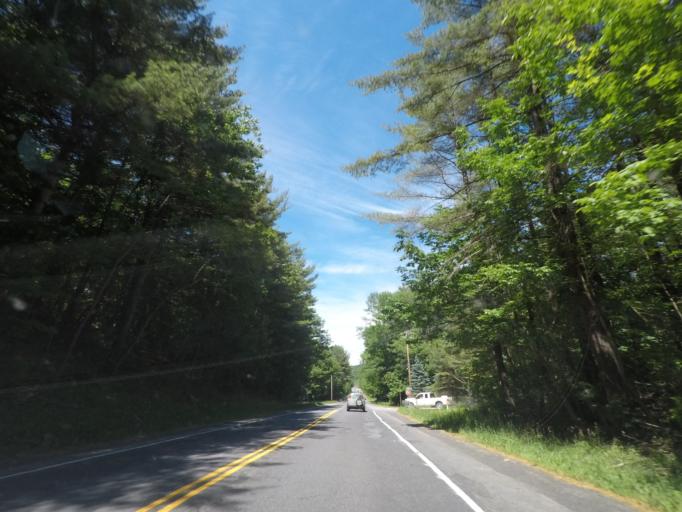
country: US
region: Massachusetts
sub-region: Berkshire County
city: Richmond
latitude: 42.3891
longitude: -73.4167
